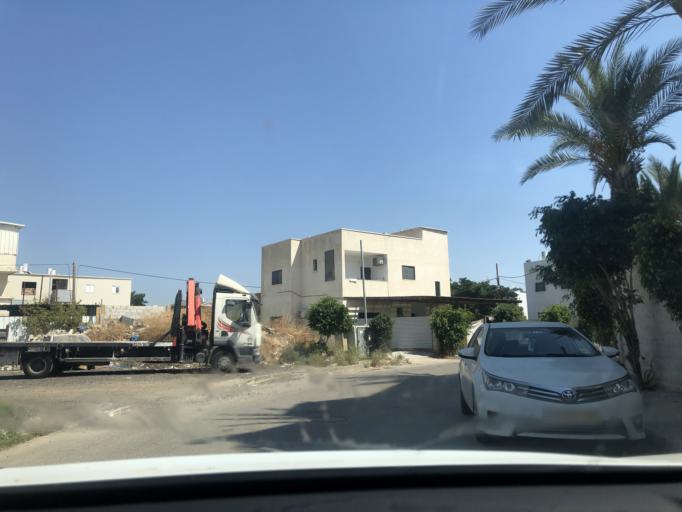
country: IL
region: Central District
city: Lod
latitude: 31.9538
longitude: 34.8767
